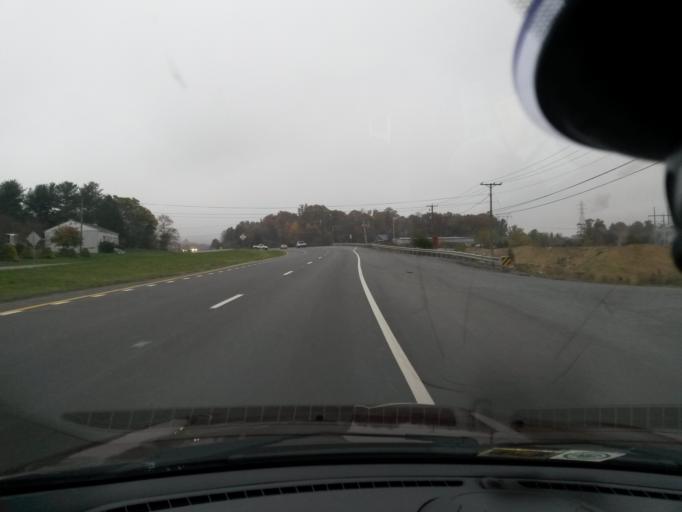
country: US
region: Virginia
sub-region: Botetourt County
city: Cloverdale
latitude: 37.3794
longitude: -79.8910
